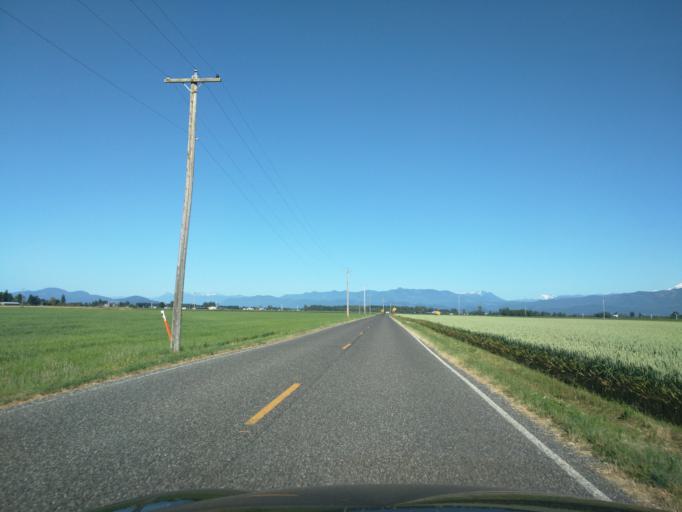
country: US
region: Washington
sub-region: Whatcom County
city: Lynden
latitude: 48.9968
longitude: -122.4447
